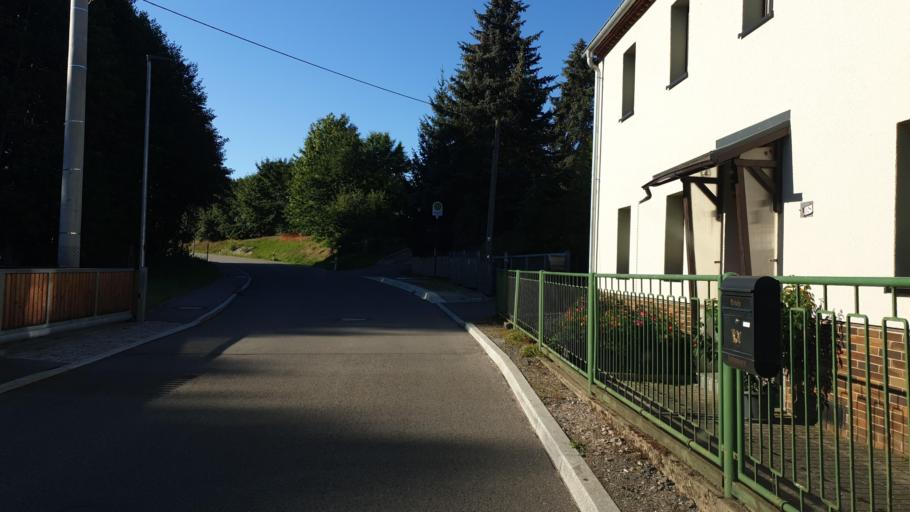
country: DE
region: Saxony
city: Lichtentanne
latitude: 50.6685
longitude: 12.4332
